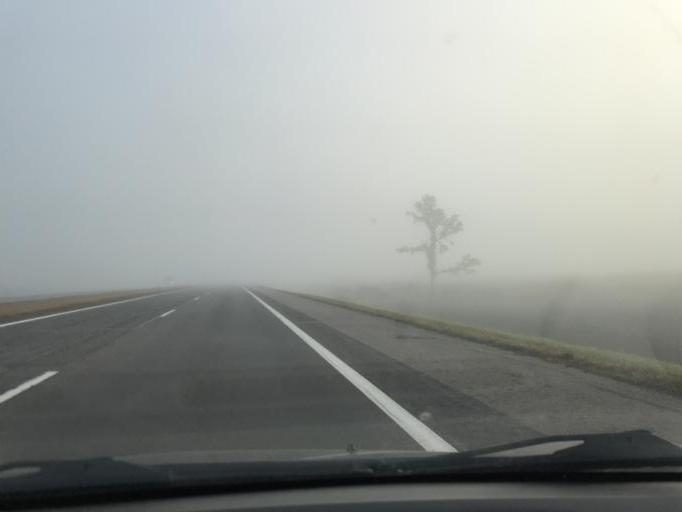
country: BY
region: Minsk
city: Zamostochcha
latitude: 53.8315
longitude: 27.8468
